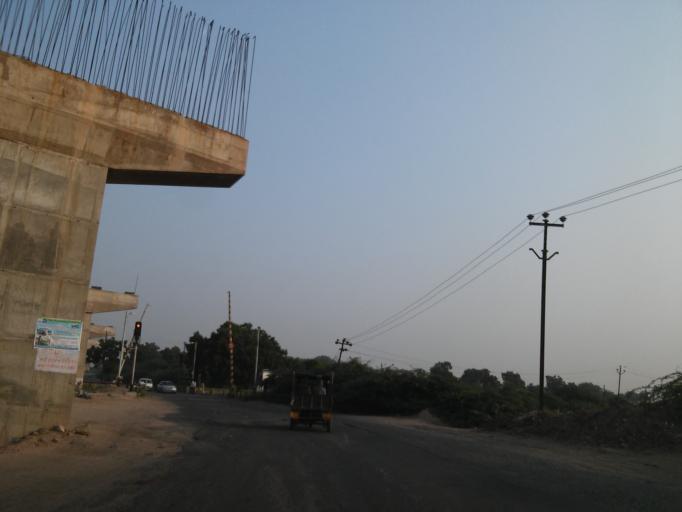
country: IN
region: Gujarat
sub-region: Kachchh
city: Bhachau
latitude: 23.3064
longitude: 70.3574
